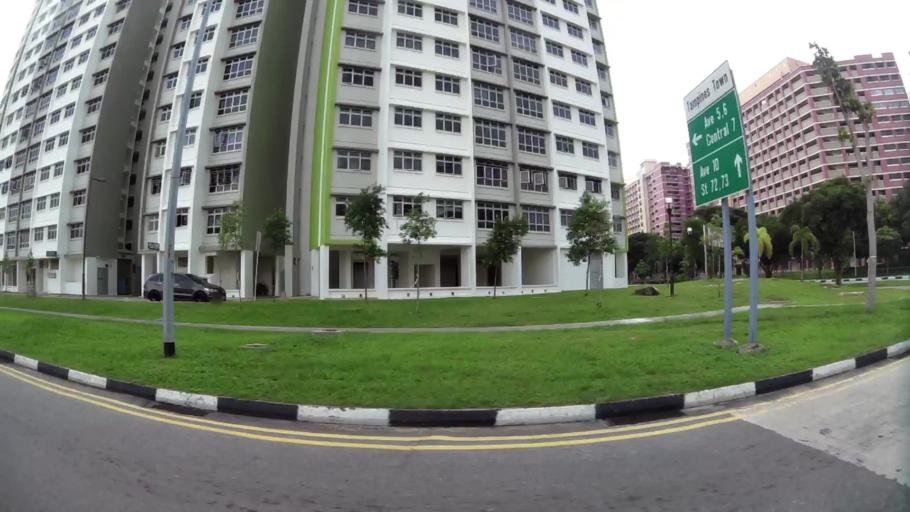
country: SG
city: Singapore
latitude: 1.3603
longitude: 103.9383
